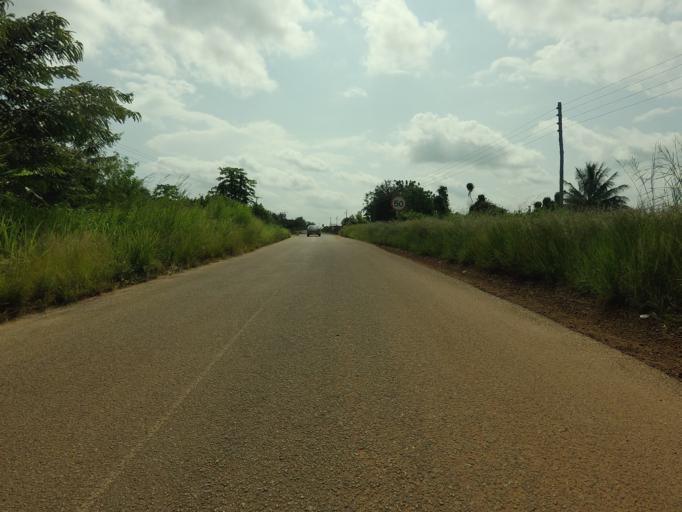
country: TG
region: Maritime
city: Lome
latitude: 6.2668
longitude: 0.9505
